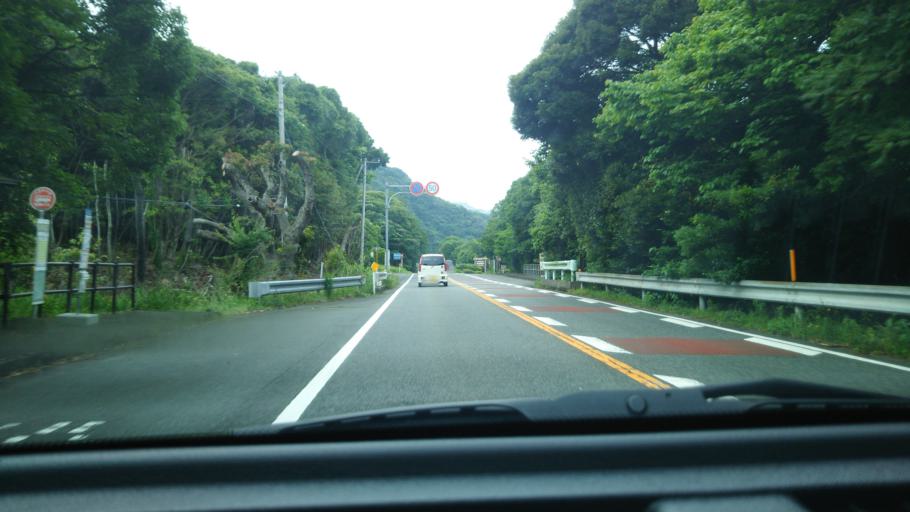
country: JP
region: Shizuoka
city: Ito
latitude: 34.8665
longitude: 139.0956
